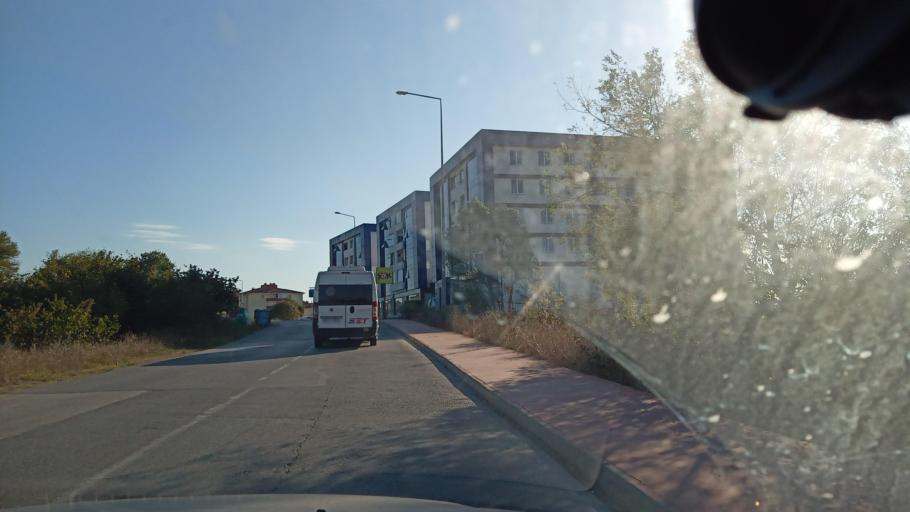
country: TR
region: Kocaeli
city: Kaymaz
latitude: 40.8591
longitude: 30.2780
